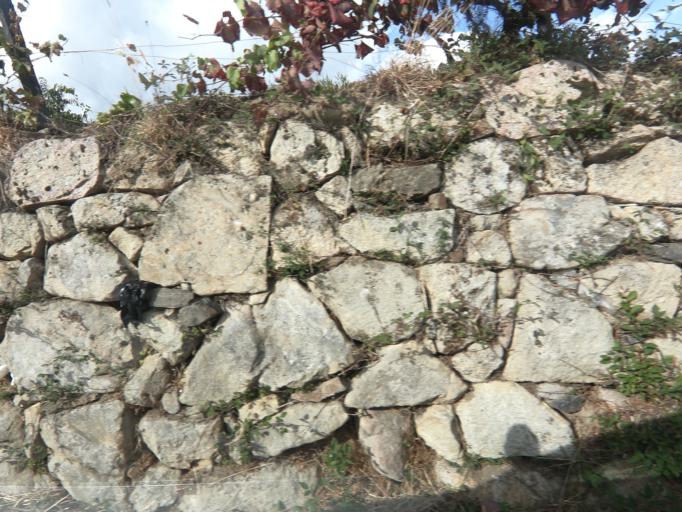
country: PT
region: Vila Real
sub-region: Vila Real
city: Vila Real
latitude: 41.3289
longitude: -7.7710
